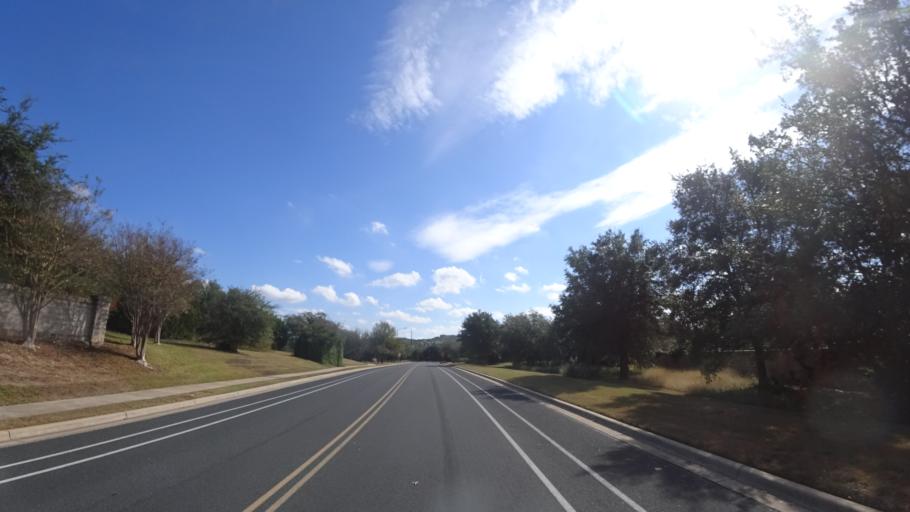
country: US
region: Texas
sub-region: Travis County
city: Hudson Bend
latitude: 30.3771
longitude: -97.9033
